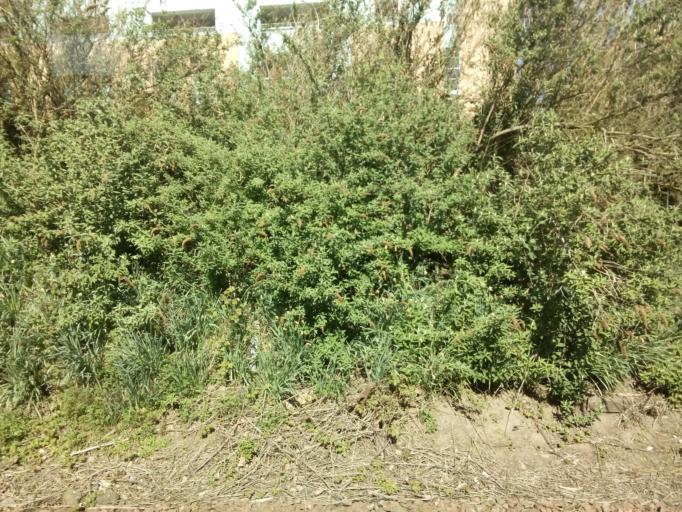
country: GB
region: Scotland
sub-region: Dundee City
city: Dundee
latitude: 56.4561
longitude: -2.9728
